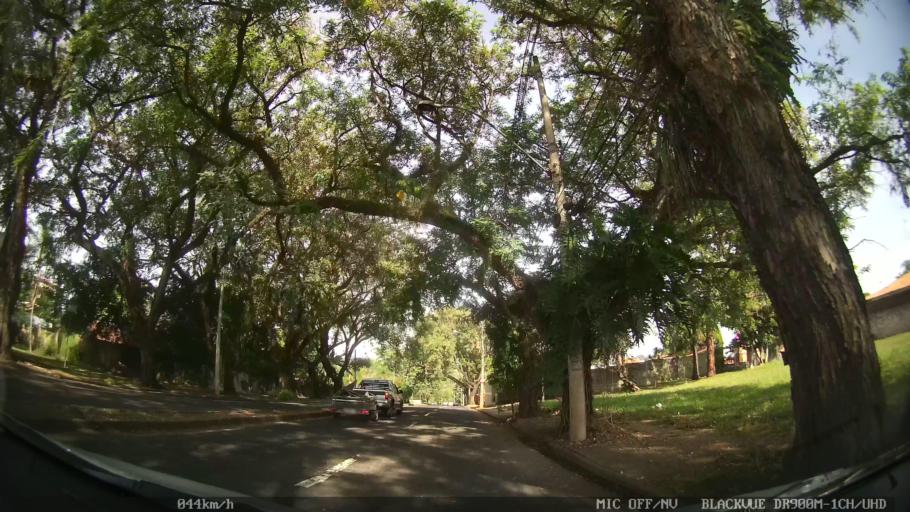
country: BR
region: Sao Paulo
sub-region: Piracicaba
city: Piracicaba
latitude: -22.7224
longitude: -47.6648
